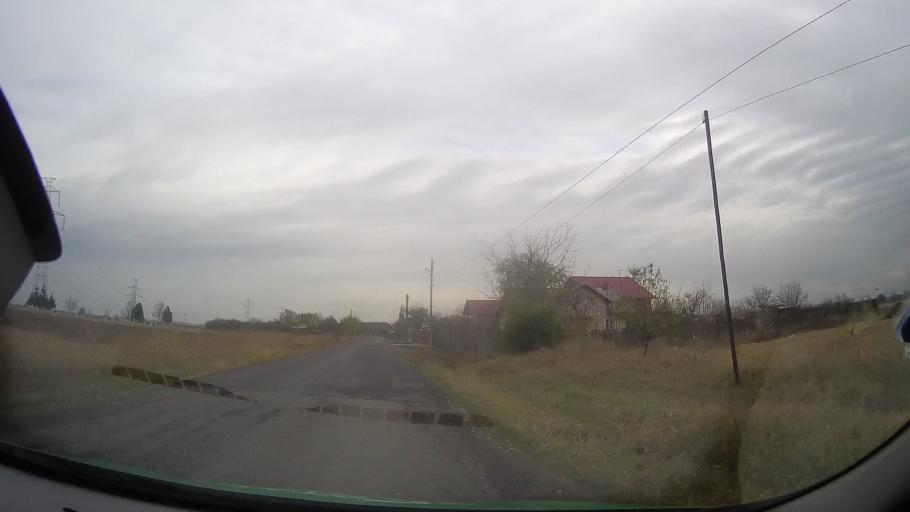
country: RO
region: Prahova
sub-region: Comuna Valea Calugareasca
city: Pantazi
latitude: 44.9253
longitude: 26.1544
